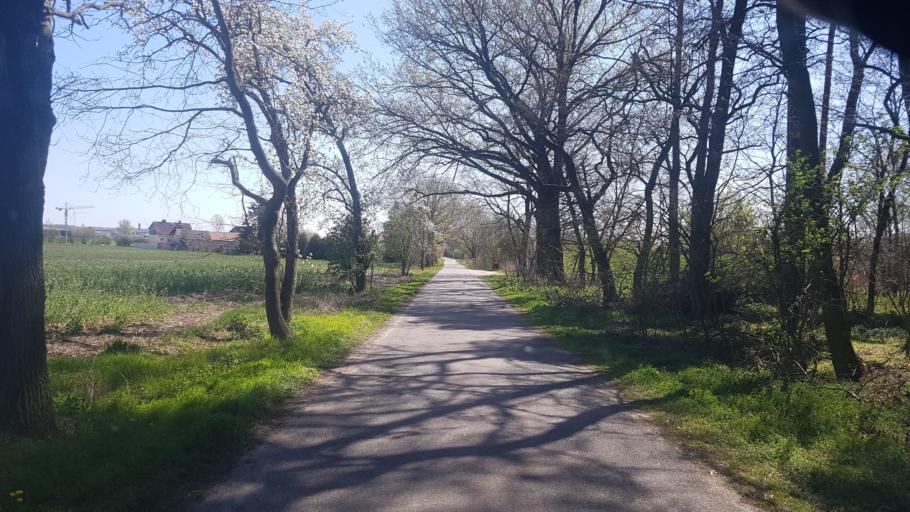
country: DE
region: Brandenburg
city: Sonnewalde
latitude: 51.7143
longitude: 13.6227
